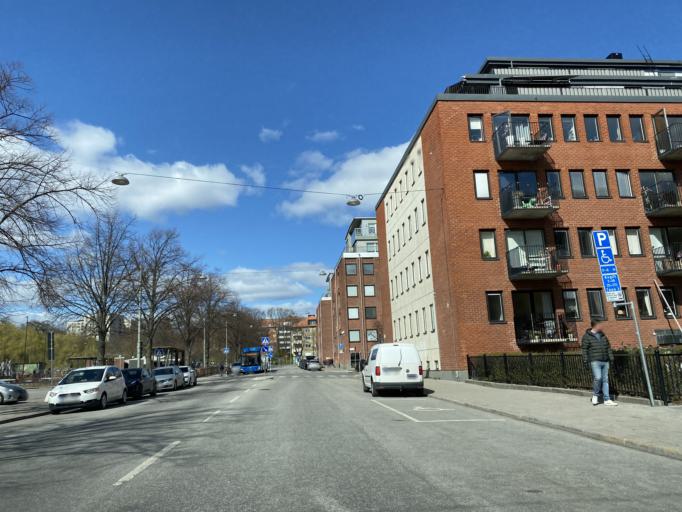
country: SE
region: Stockholm
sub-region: Stockholms Kommun
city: OEstermalm
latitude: 59.3415
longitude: 18.1110
